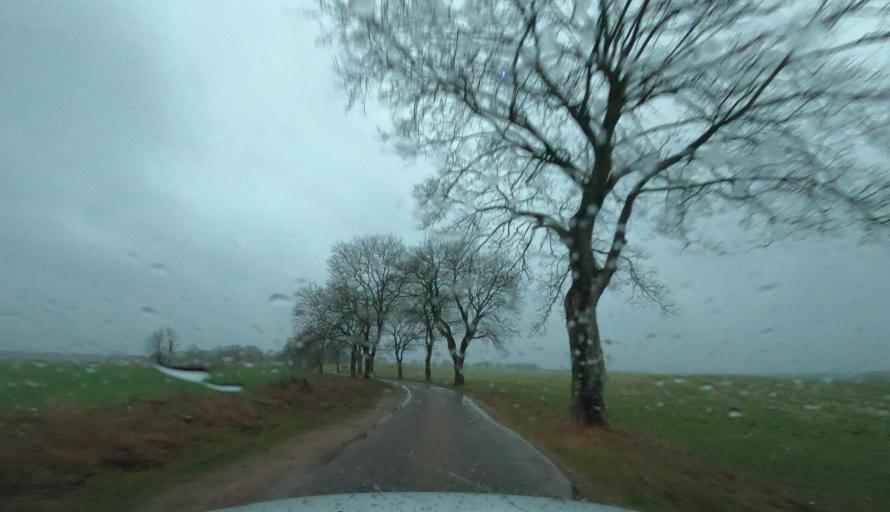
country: PL
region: West Pomeranian Voivodeship
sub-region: Powiat szczecinecki
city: Borne Sulinowo
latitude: 53.7069
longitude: 16.5304
